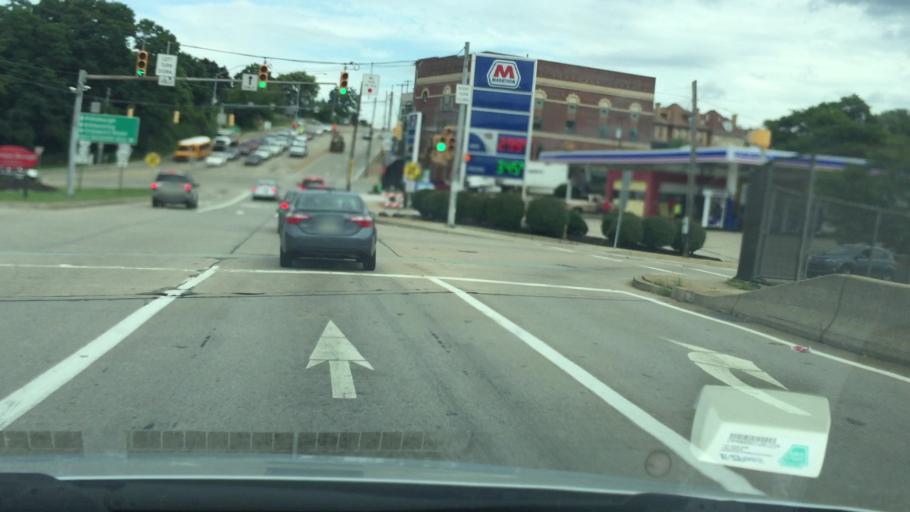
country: US
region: Pennsylvania
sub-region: Allegheny County
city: Tarentum
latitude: 40.6010
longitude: -79.7569
